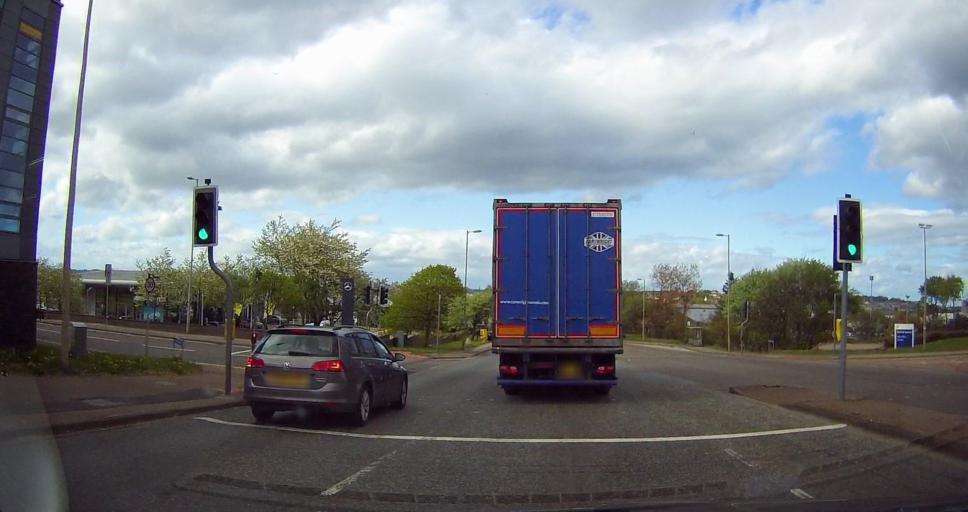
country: GB
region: Scotland
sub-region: Aberdeen City
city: Aberdeen
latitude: 57.1219
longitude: -2.0888
